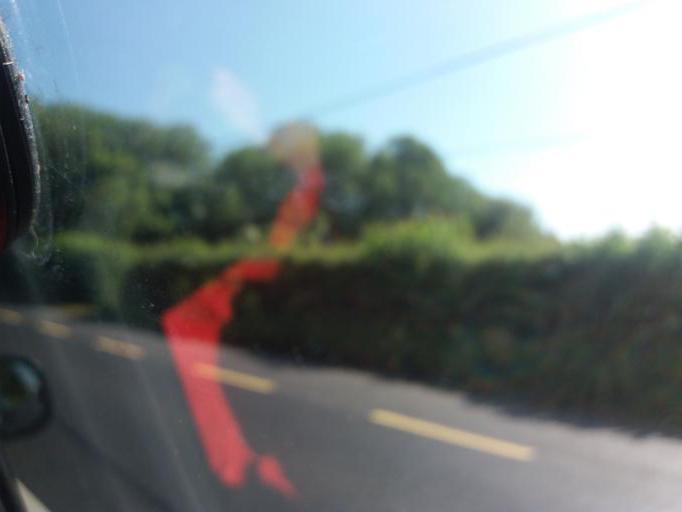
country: IE
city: Kentstown
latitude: 53.5950
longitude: -6.4664
